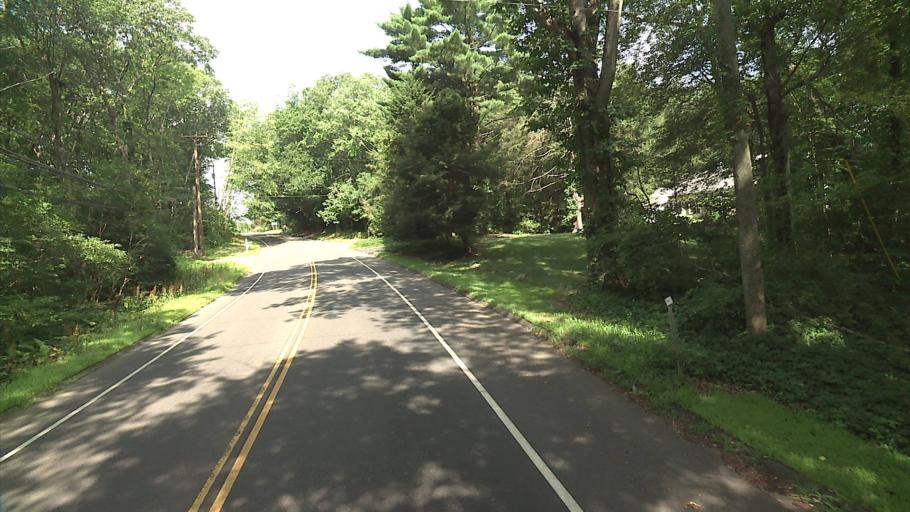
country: US
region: Connecticut
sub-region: New Haven County
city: Woodbridge
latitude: 41.3322
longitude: -73.0379
